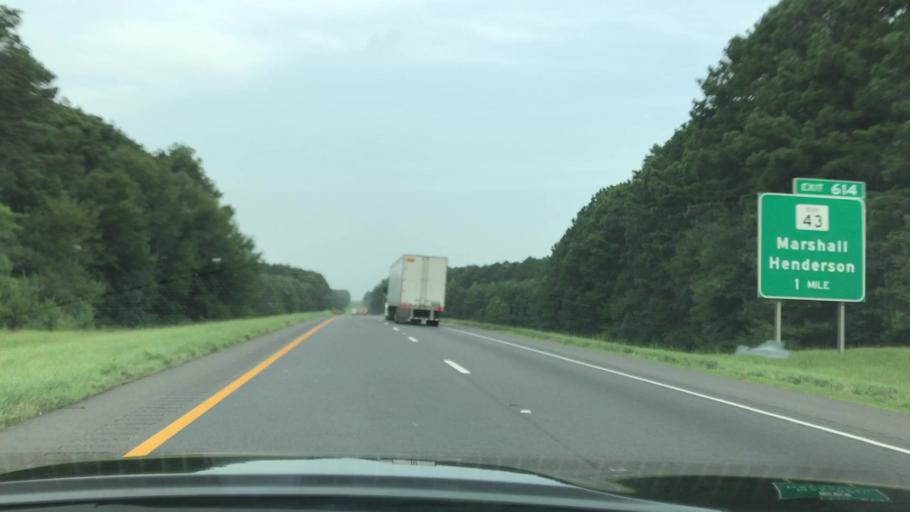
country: US
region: Texas
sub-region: Harrison County
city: Marshall
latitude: 32.4900
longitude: -94.3876
